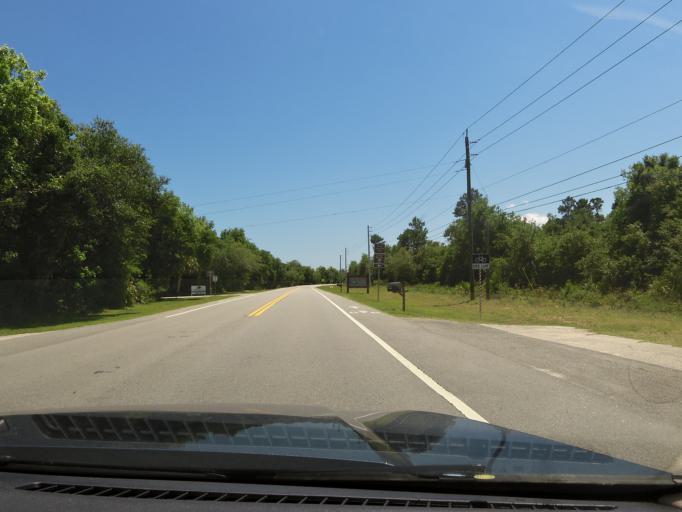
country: US
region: Florida
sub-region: Flagler County
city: Flagler Beach
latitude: 29.4309
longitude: -81.1540
